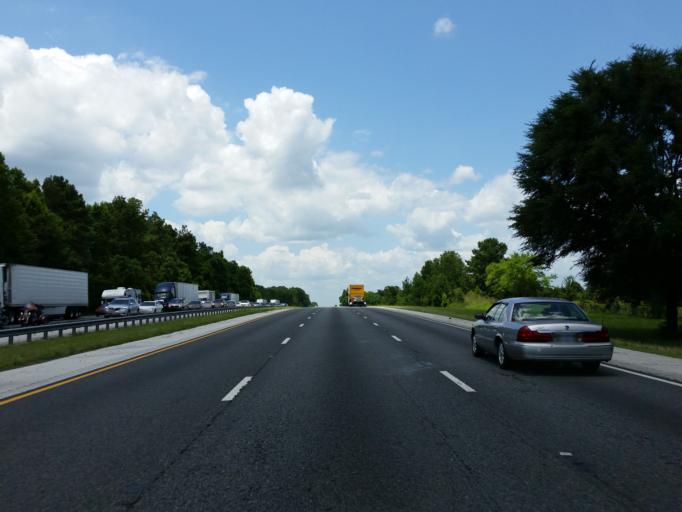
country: US
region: Florida
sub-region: Marion County
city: Citra
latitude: 29.3816
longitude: -82.2333
